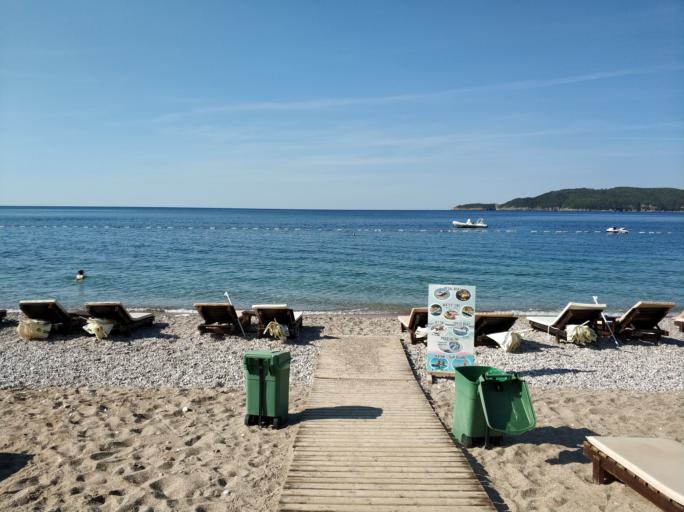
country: ME
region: Budva
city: Budva
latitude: 42.2753
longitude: 18.8869
